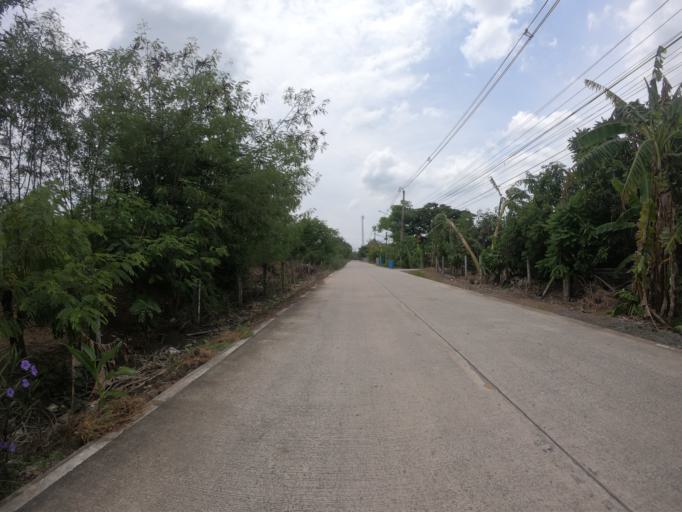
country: TH
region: Pathum Thani
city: Ban Lam Luk Ka
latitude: 14.0037
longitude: 100.8660
